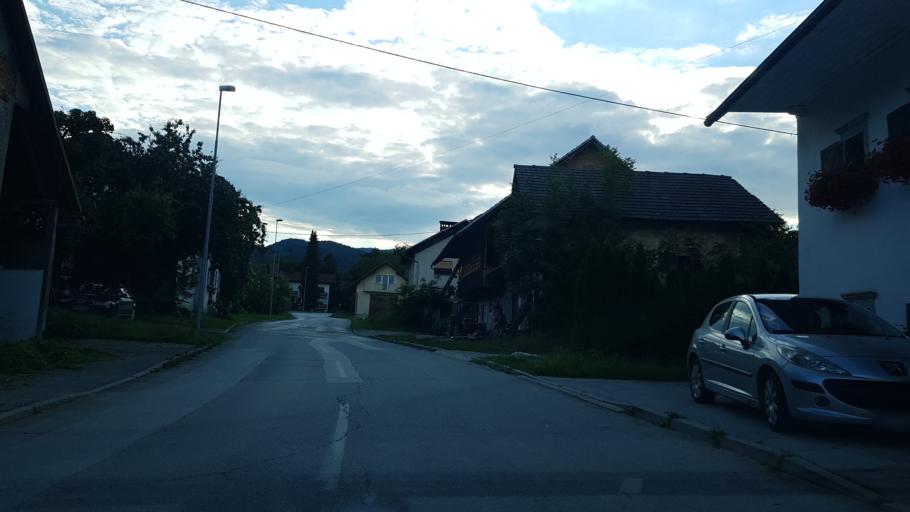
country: SI
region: Naklo
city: Naklo
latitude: 46.2609
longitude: 14.2858
